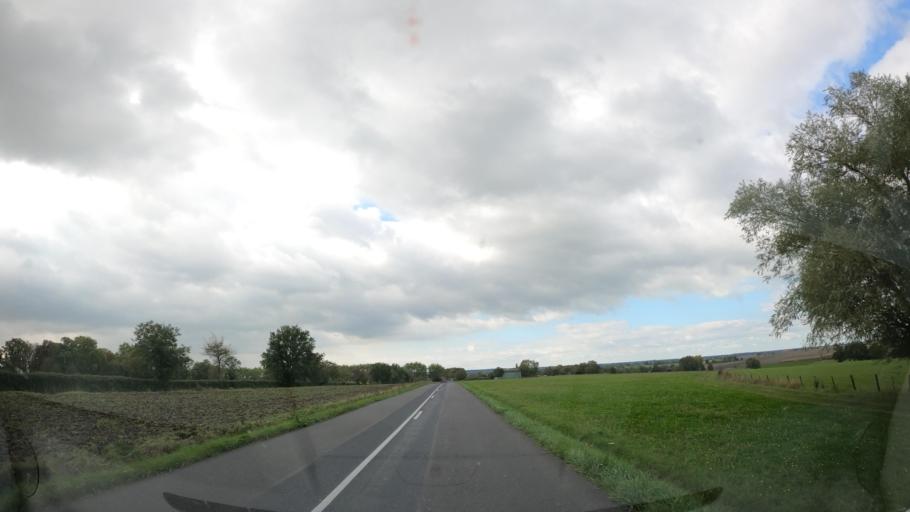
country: FR
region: Auvergne
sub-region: Departement de l'Allier
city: Lapalisse
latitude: 46.3688
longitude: 3.6176
